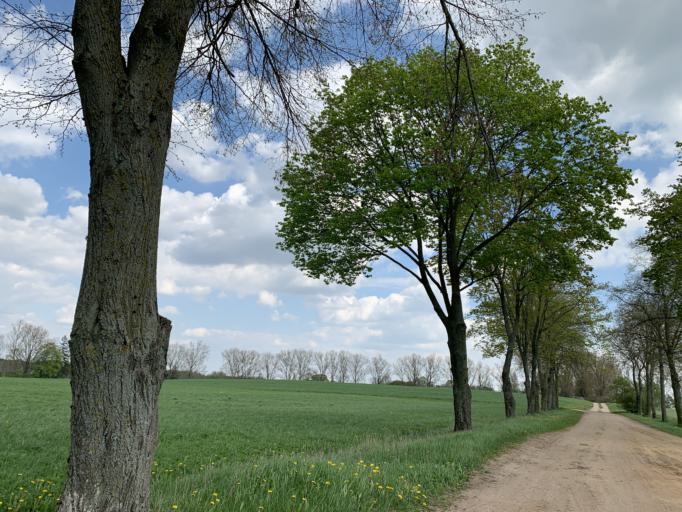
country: BY
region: Minsk
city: Nyasvizh
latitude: 53.2454
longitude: 26.6909
